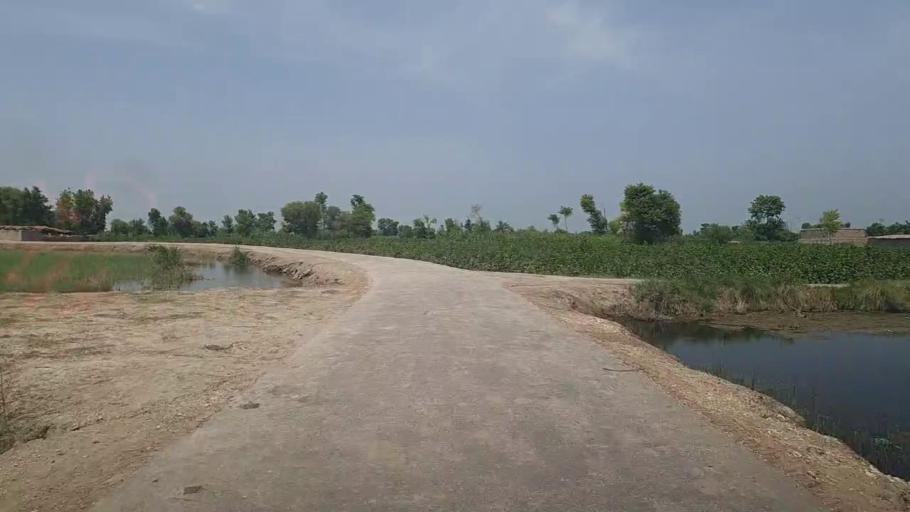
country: PK
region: Sindh
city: Ubauro
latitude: 28.1912
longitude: 69.7711
